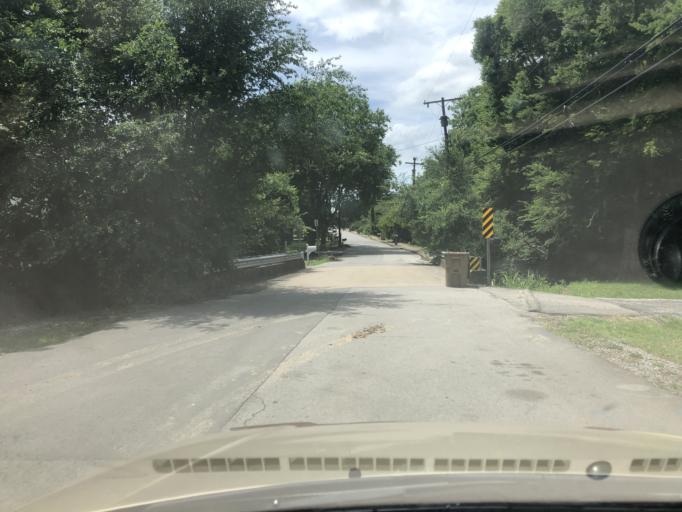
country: US
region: Tennessee
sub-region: Davidson County
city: Goodlettsville
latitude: 36.2569
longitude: -86.7098
